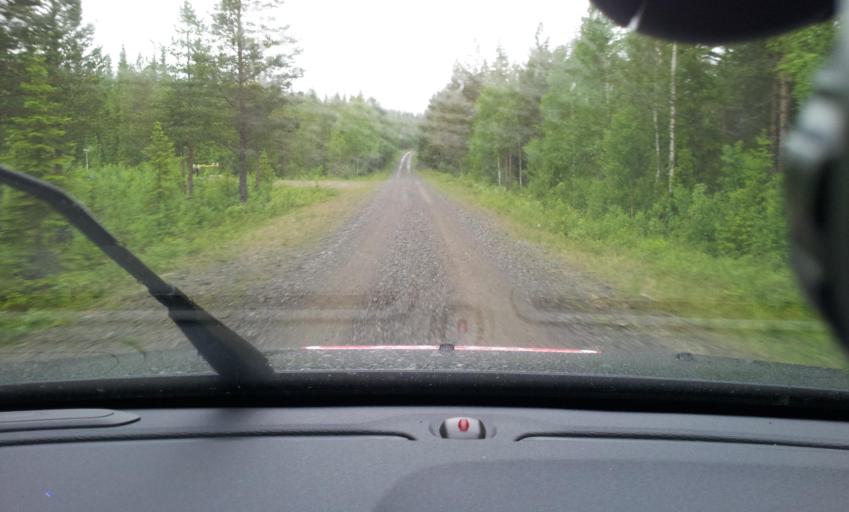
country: SE
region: Jaemtland
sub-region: Are Kommun
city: Are
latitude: 63.1911
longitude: 13.1857
